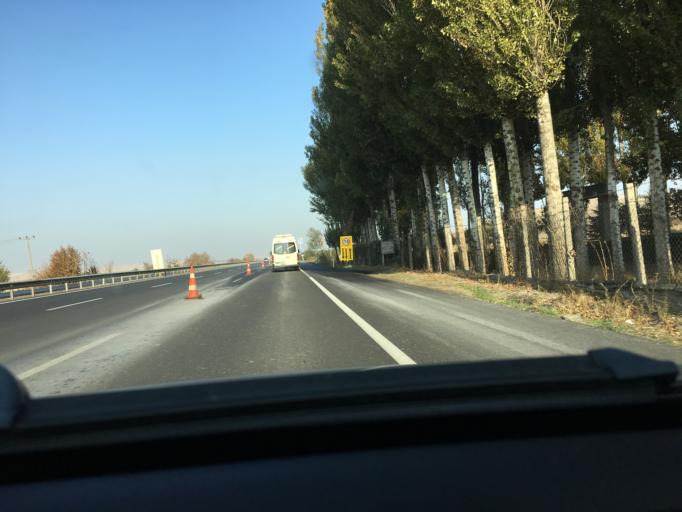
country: TR
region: Ankara
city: Temelli
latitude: 39.6918
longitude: 32.2560
